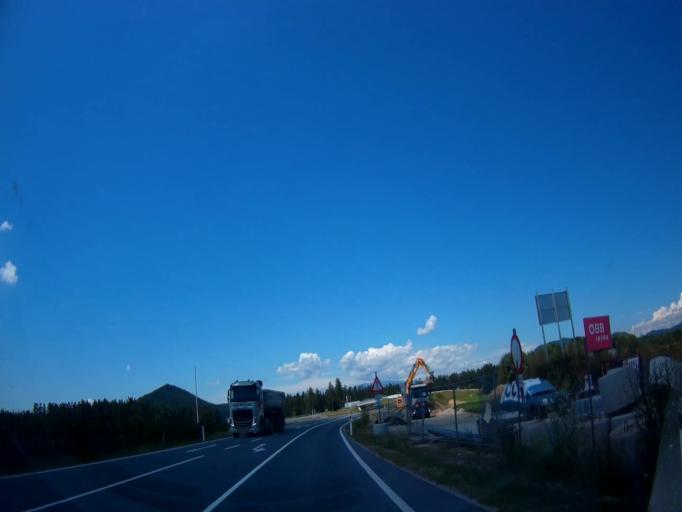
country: AT
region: Carinthia
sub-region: Politischer Bezirk Volkermarkt
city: Bleiburg/Pliberk
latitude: 46.6073
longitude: 14.7836
